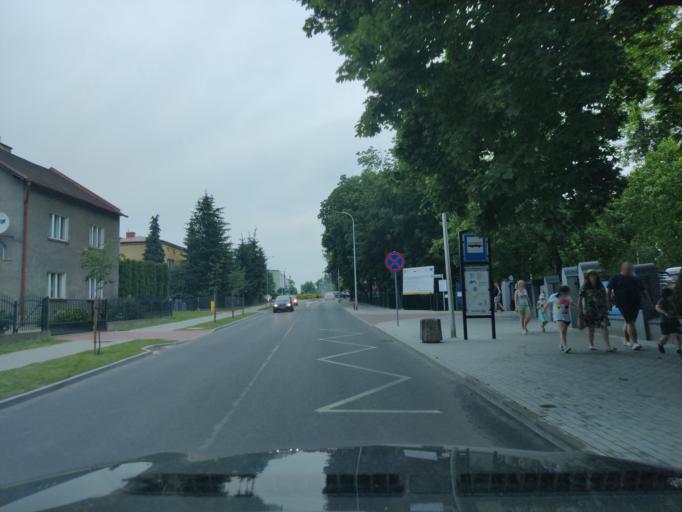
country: PL
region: Warmian-Masurian Voivodeship
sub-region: Powiat dzialdowski
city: Dzialdowo
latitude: 53.2374
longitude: 20.1857
